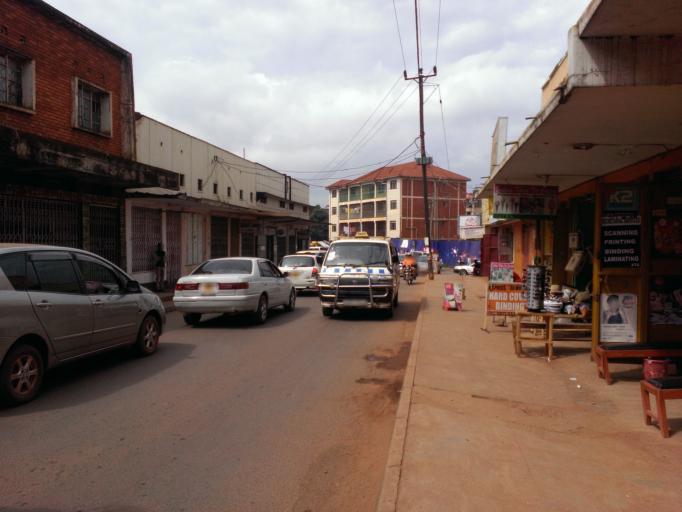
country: UG
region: Central Region
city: Kampala Central Division
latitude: 0.3111
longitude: 32.5574
